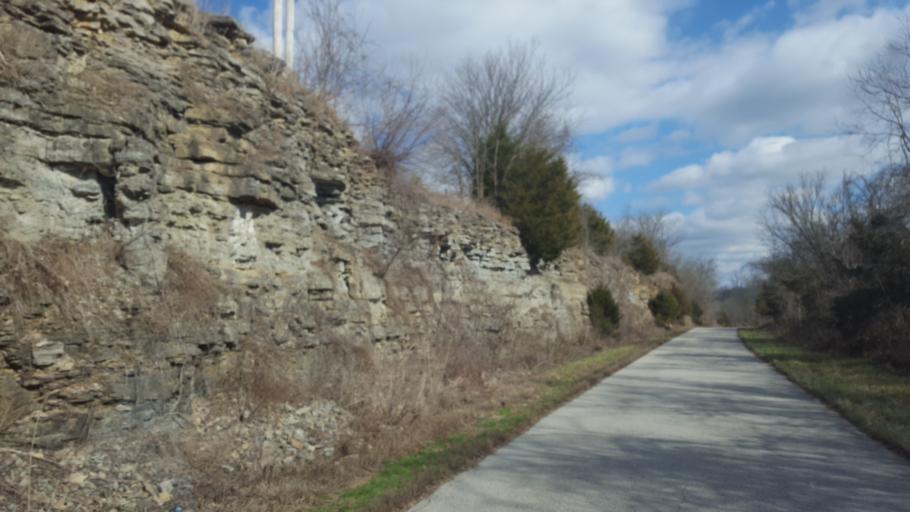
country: US
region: Kentucky
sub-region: Franklin County
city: Frankfort
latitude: 38.3568
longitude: -84.8841
